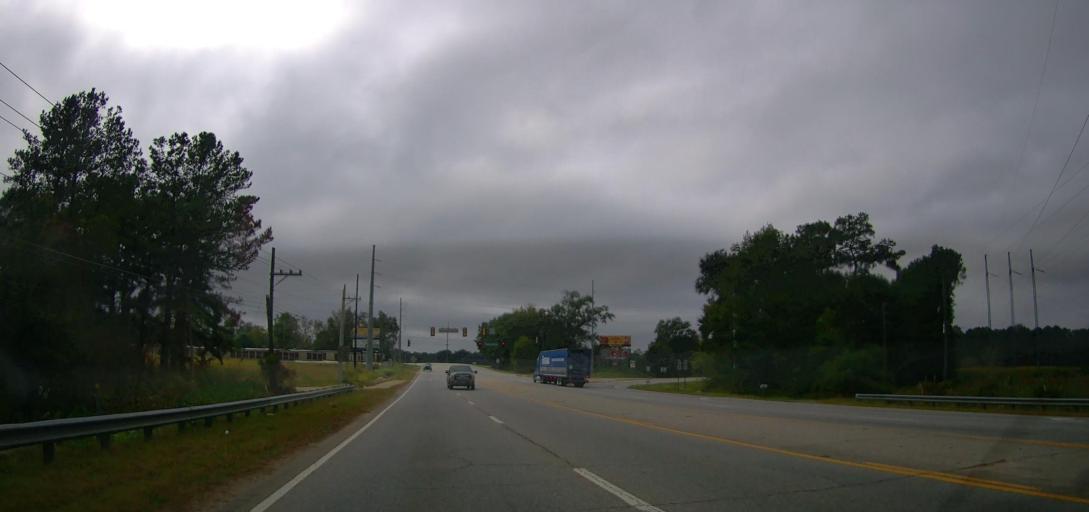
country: US
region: Georgia
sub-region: Thomas County
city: Thomasville
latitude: 30.8743
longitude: -83.9374
